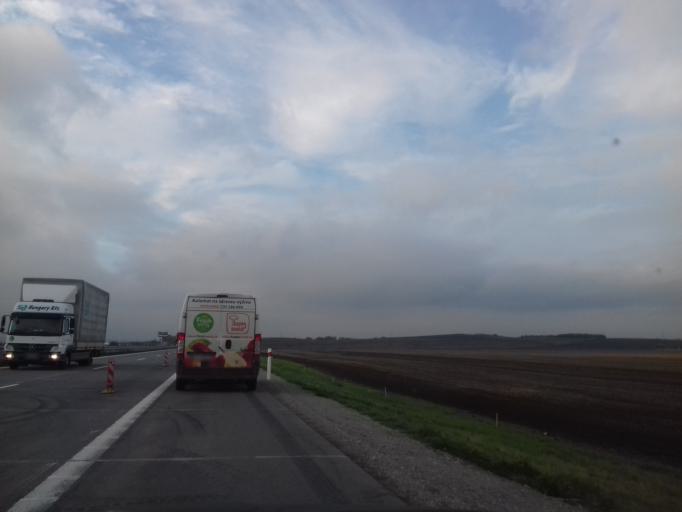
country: CZ
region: South Moravian
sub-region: Okres Brno-Venkov
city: Blucina
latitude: 49.0481
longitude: 16.6757
